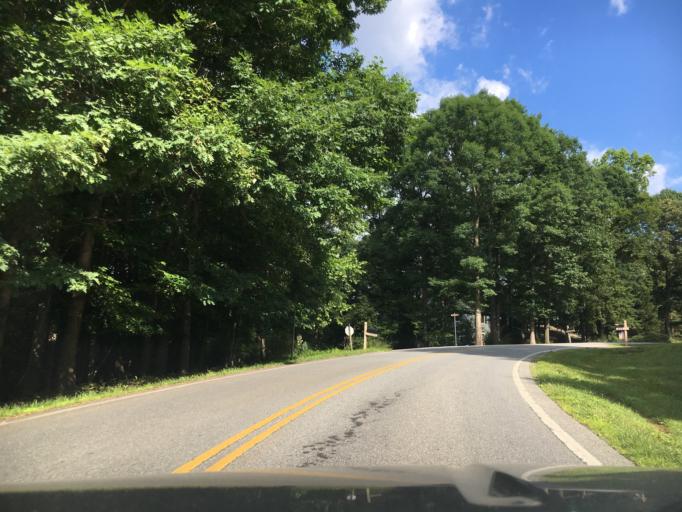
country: US
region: Virginia
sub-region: Bedford County
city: Forest
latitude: 37.3889
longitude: -79.2551
